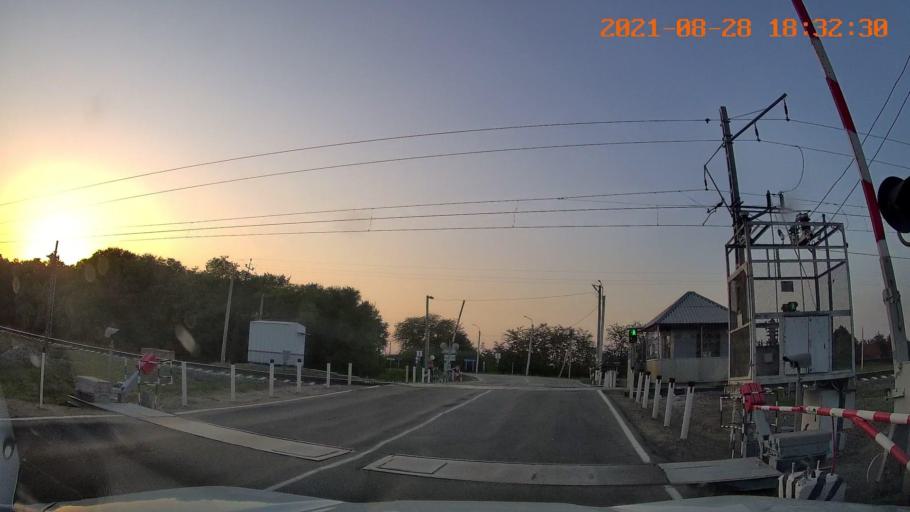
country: RU
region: Adygeya
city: Giaginskaya
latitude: 44.8765
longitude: 40.1897
